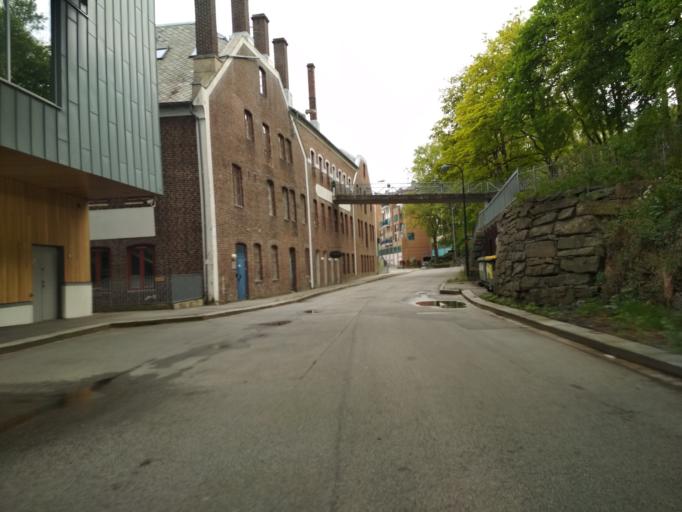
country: NO
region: Rogaland
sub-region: Stavanger
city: Stavanger
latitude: 58.9766
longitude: 5.7214
